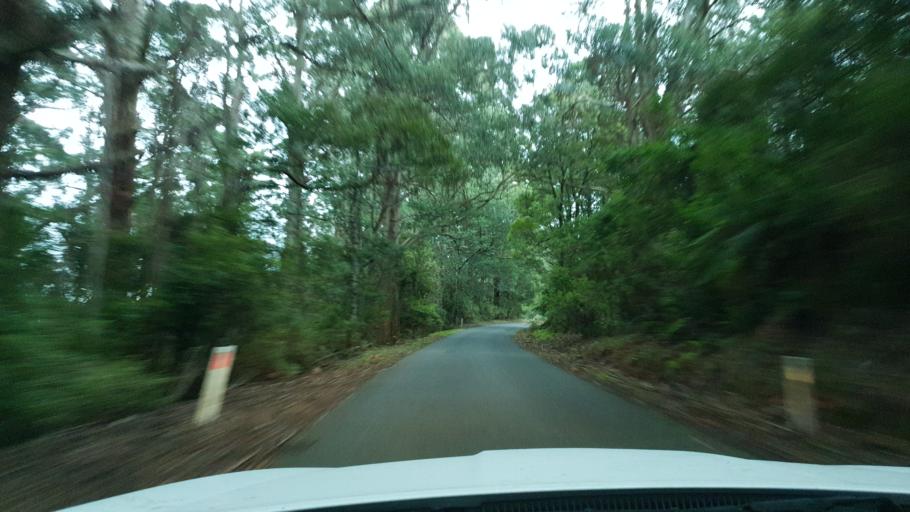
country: AU
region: Victoria
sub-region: Latrobe
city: Traralgon
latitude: -38.4230
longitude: 146.5822
